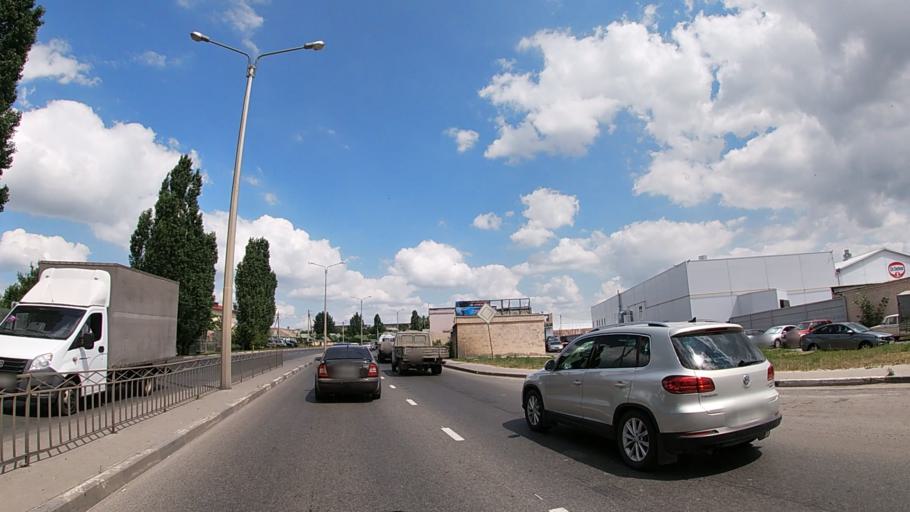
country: RU
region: Belgorod
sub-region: Belgorodskiy Rayon
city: Belgorod
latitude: 50.6106
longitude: 36.5339
